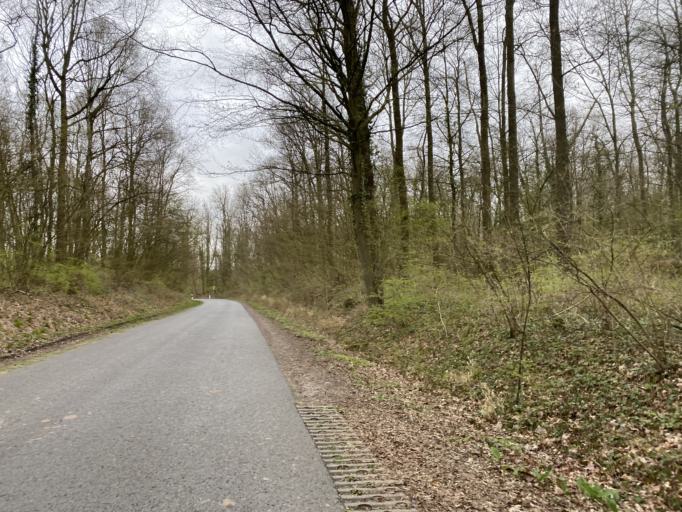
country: DE
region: North Rhine-Westphalia
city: Ahlen
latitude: 51.6835
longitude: 7.9127
